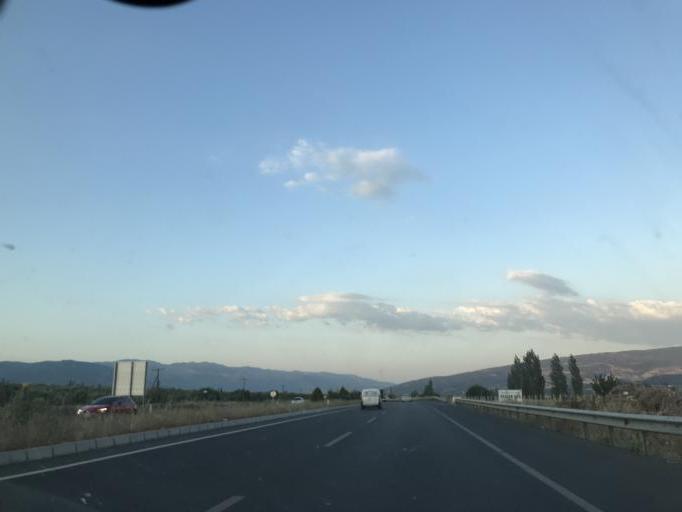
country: TR
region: Aydin
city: Horsunlu
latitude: 37.9178
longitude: 28.6261
